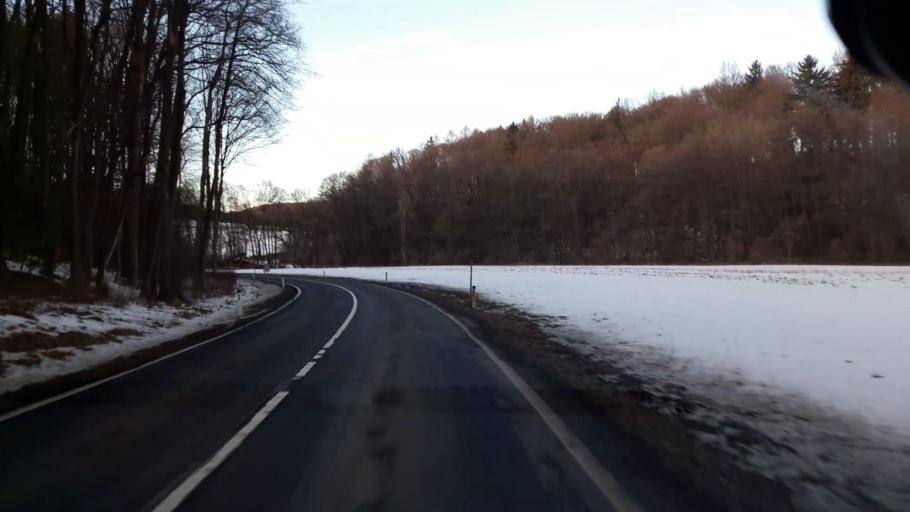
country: AT
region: Lower Austria
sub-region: Politischer Bezirk Wien-Umgebung
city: Mauerbach
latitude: 48.2599
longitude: 16.1696
